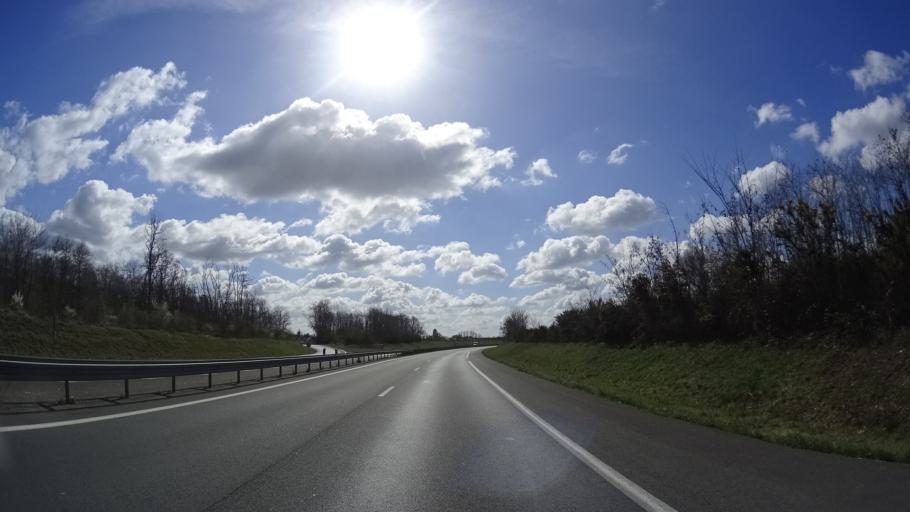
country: FR
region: Pays de la Loire
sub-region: Departement de Maine-et-Loire
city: Saint-Jean
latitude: 47.3031
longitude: -0.3911
